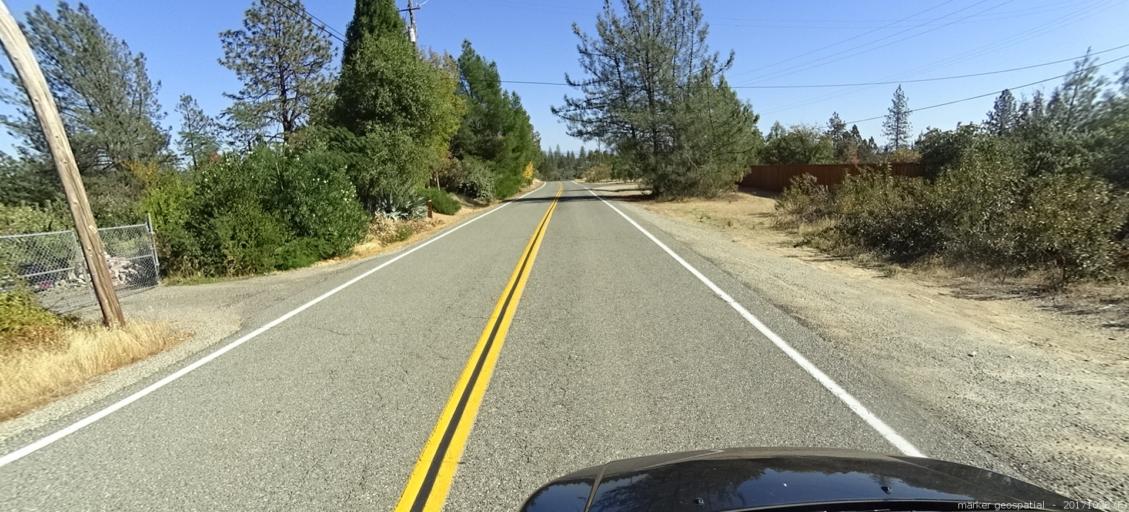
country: US
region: California
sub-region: Shasta County
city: Shasta
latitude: 40.6194
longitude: -122.4716
